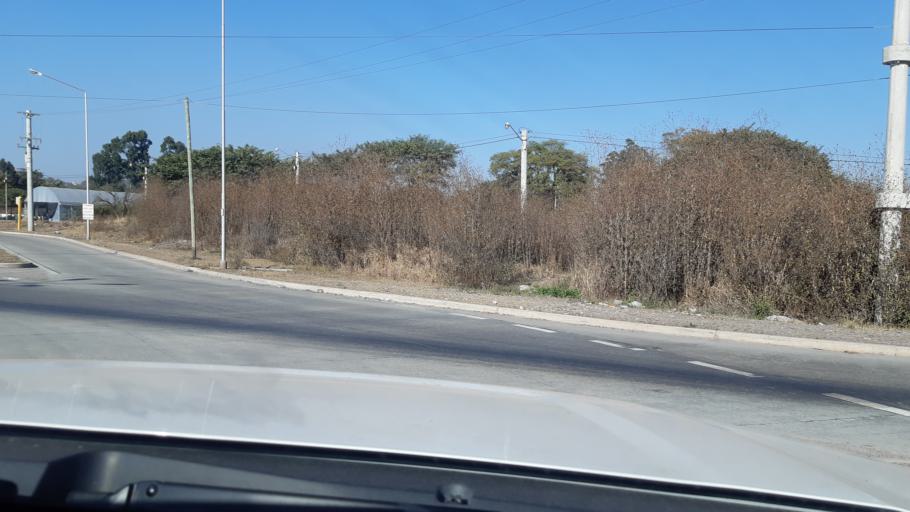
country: AR
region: Jujuy
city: Palpala
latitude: -24.2254
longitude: -65.2429
